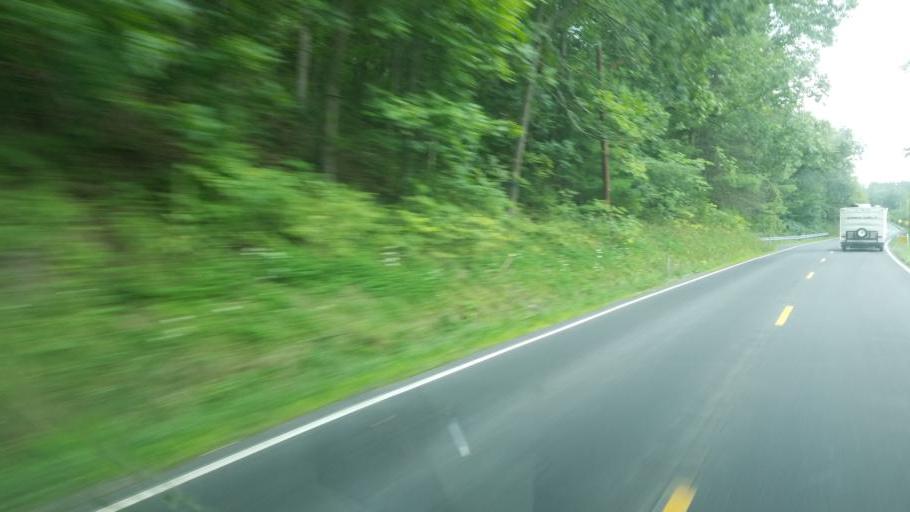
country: US
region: West Virginia
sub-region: Mineral County
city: Fort Ashby
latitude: 39.5360
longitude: -78.5446
